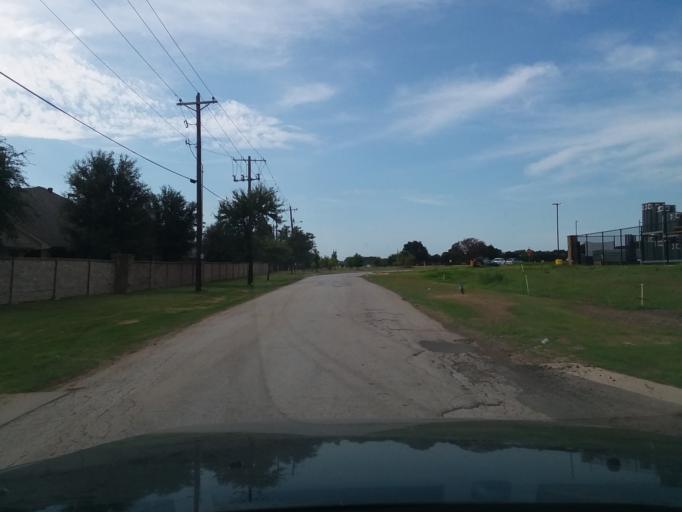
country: US
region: Texas
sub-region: Denton County
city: Bartonville
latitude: 33.1029
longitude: -97.1312
